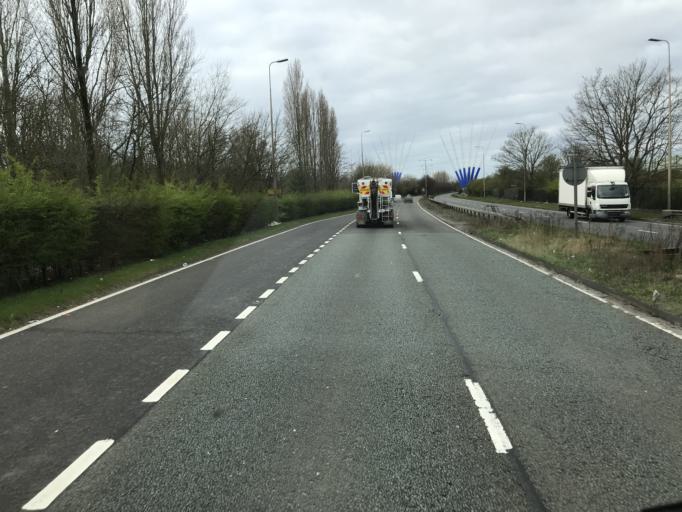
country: GB
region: England
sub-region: Borough of Halton
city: Hale
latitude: 53.3486
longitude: -2.8204
